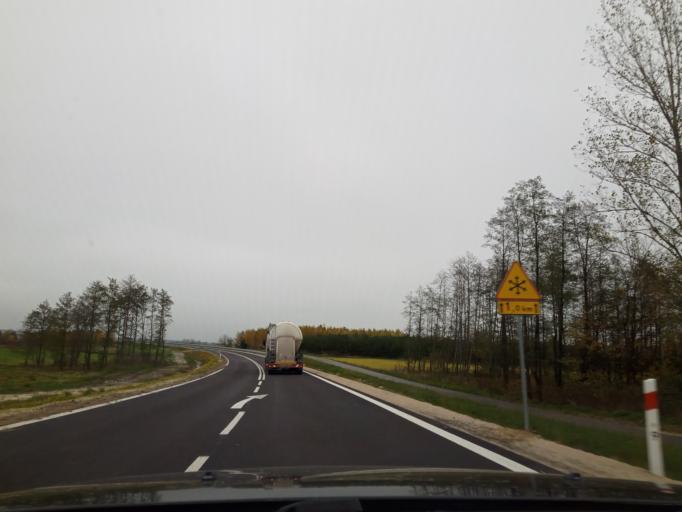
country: PL
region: Swietokrzyskie
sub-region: Powiat jedrzejowski
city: Jedrzejow
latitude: 50.6241
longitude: 20.3229
